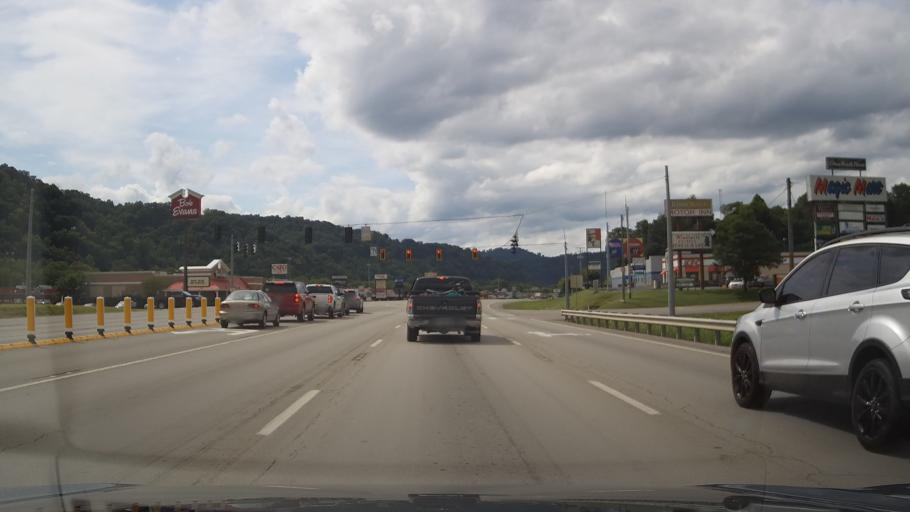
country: US
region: Kentucky
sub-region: Pike County
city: Coal Run Village
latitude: 37.5219
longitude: -82.5699
